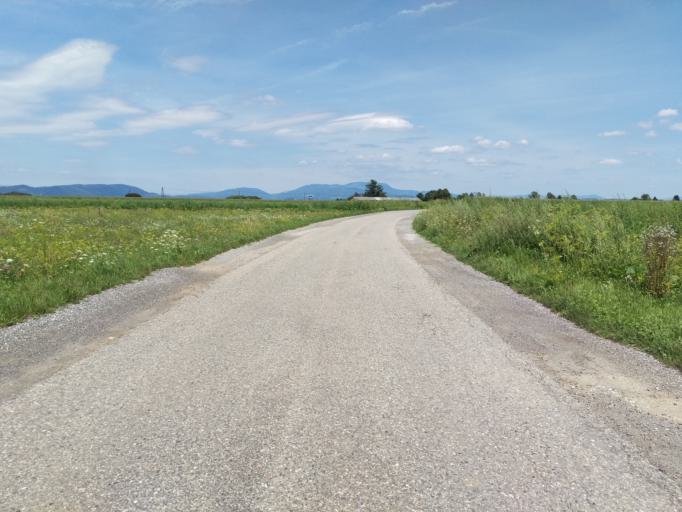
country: AT
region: Styria
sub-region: Politischer Bezirk Graz-Umgebung
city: Kalsdorf bei Graz
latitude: 46.9710
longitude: 15.4472
